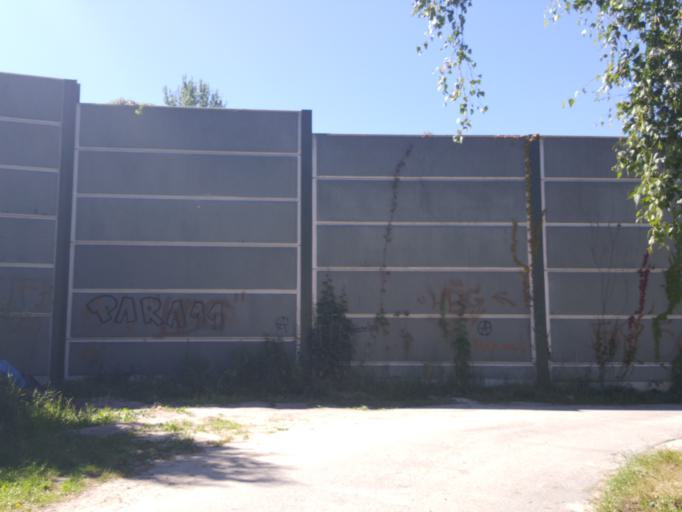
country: DE
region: Hamburg
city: Bergedorf
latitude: 53.4772
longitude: 10.2312
